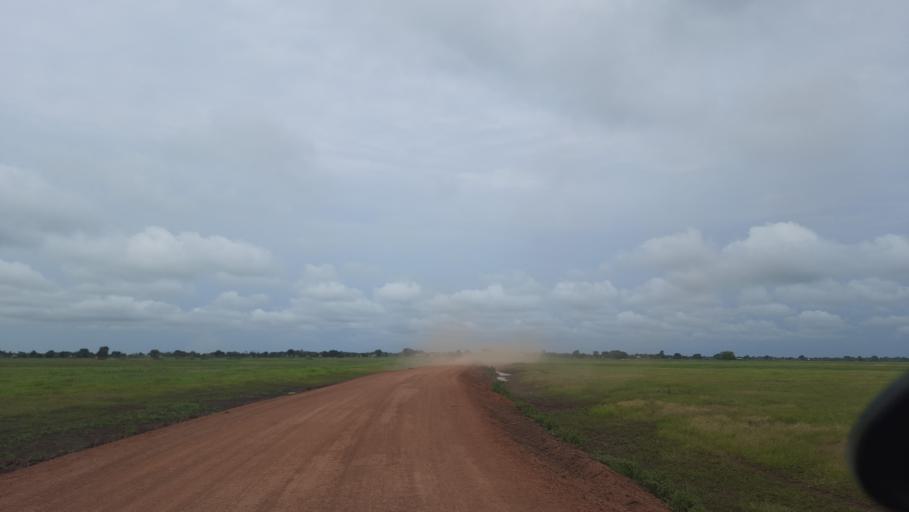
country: ET
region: Gambela
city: Gambela
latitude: 8.3365
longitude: 33.7760
